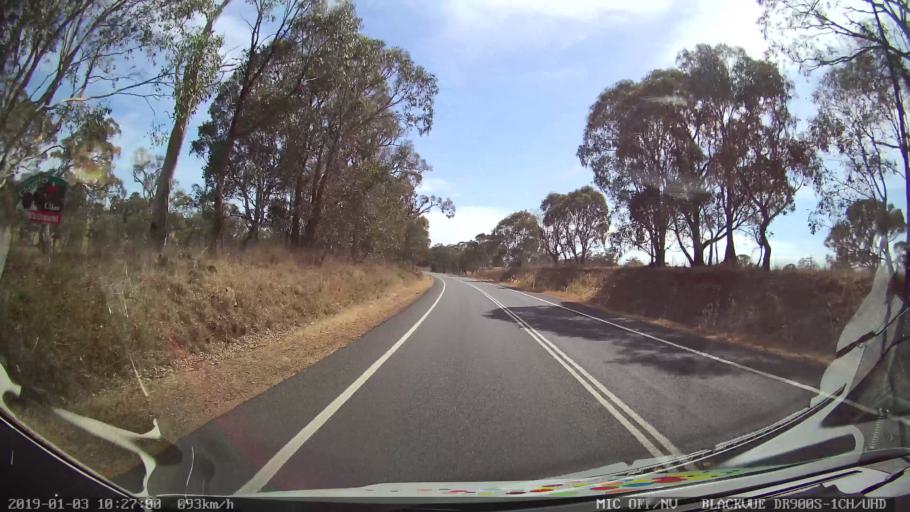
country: AU
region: New South Wales
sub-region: Young
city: Young
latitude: -34.4075
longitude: 148.2557
